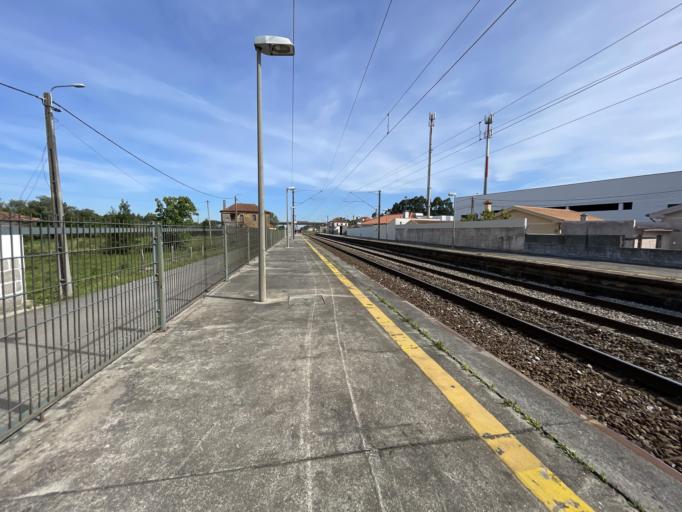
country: PT
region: Aveiro
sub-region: Ovar
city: Cortegaca
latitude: 40.9400
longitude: -8.6300
